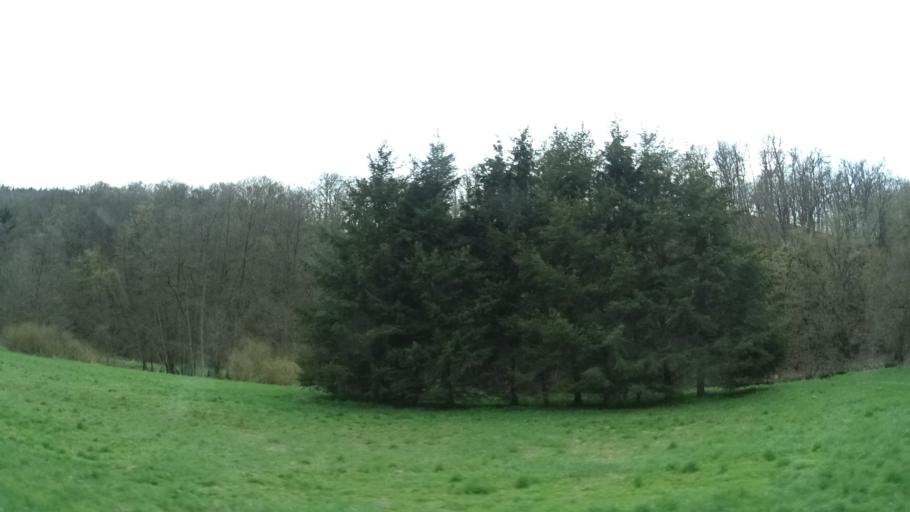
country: DE
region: Rheinland-Pfalz
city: Kellenbach
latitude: 49.8401
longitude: 7.4876
